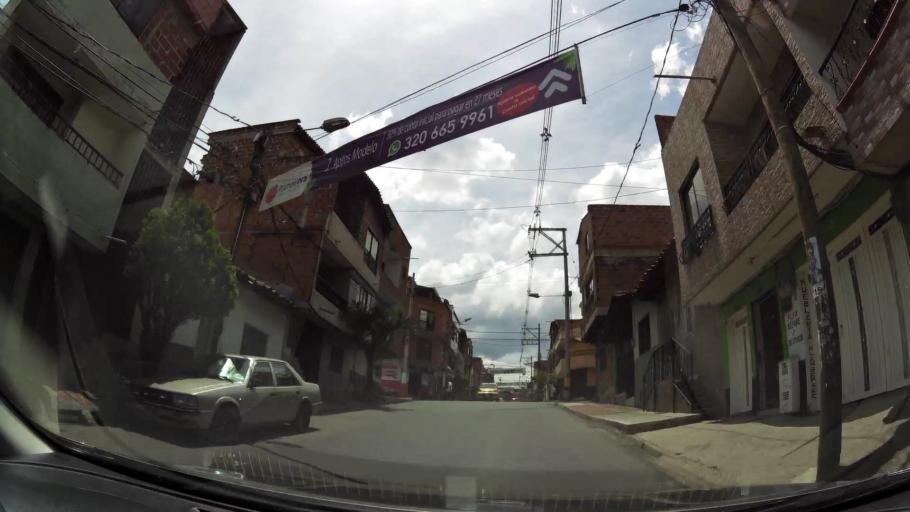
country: CO
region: Antioquia
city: Bello
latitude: 6.3432
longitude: -75.5642
